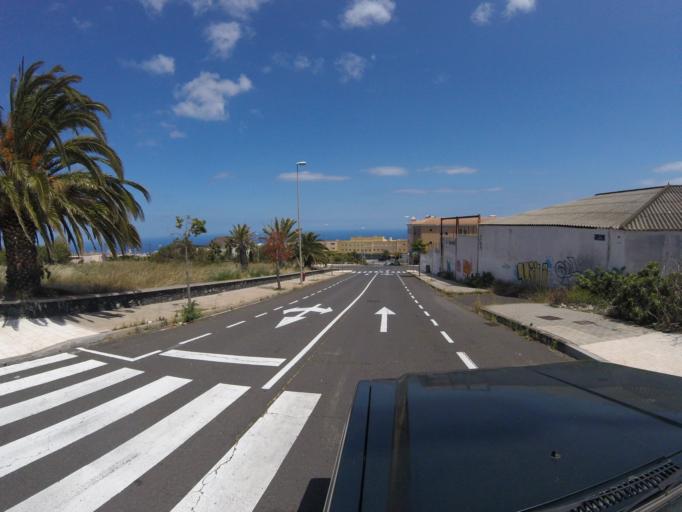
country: ES
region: Canary Islands
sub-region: Provincia de Santa Cruz de Tenerife
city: La Laguna
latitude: 28.4443
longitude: -16.3127
